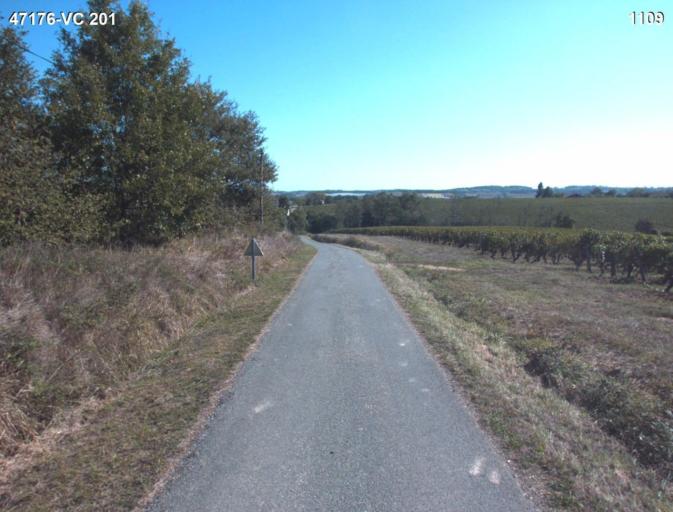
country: FR
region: Aquitaine
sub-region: Departement du Lot-et-Garonne
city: Vianne
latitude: 44.2137
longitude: 0.3012
